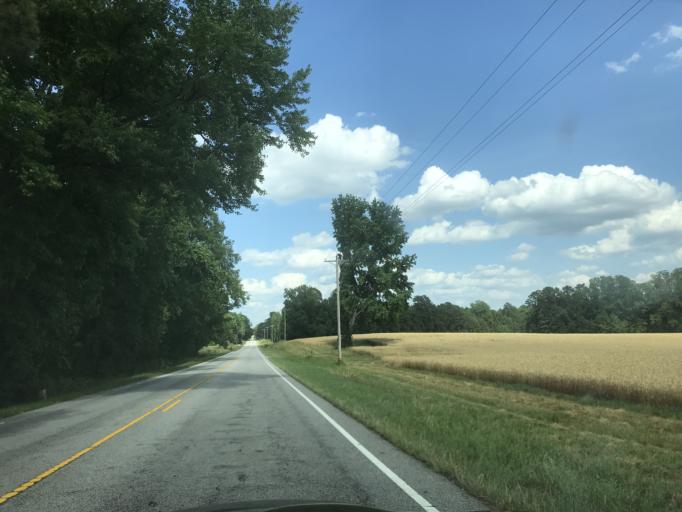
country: US
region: North Carolina
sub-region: Wake County
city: Rolesville
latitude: 35.9642
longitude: -78.4273
